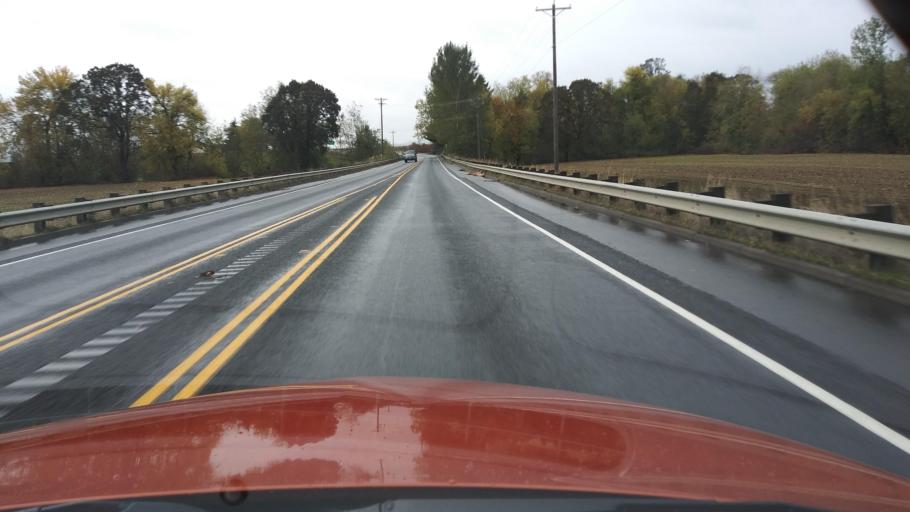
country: US
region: Oregon
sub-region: Washington County
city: Cornelius
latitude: 45.5561
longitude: -123.0611
